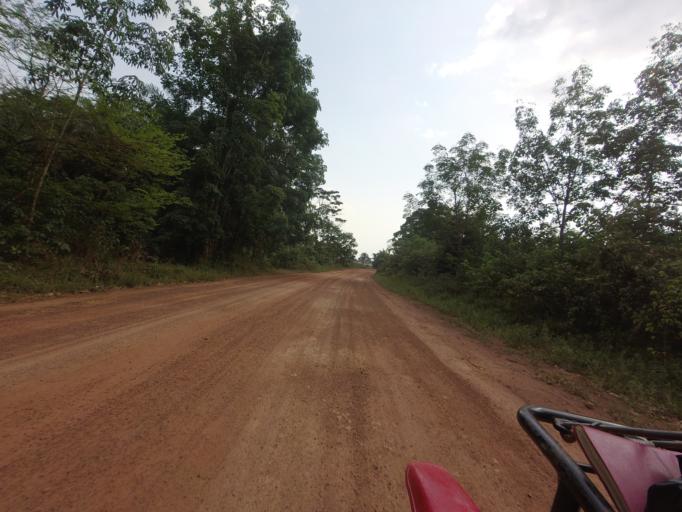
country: LR
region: Nimba
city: Sanniquellie
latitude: 7.3801
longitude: -8.6774
